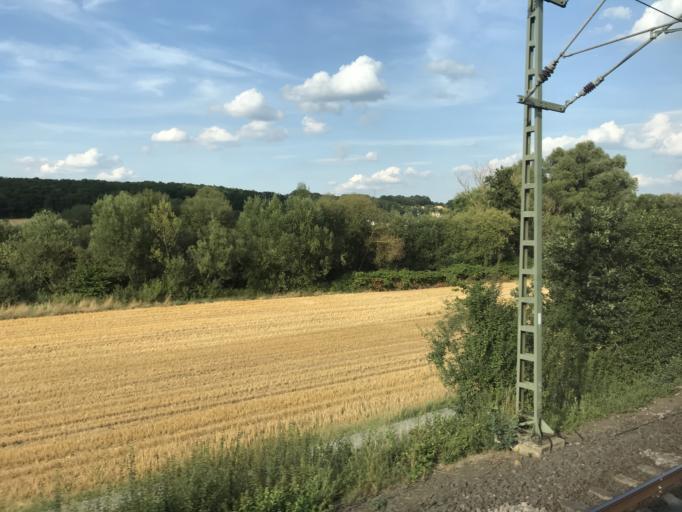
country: DE
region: Hesse
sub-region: Regierungsbezirk Giessen
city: Steeden
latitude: 50.3944
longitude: 8.1133
